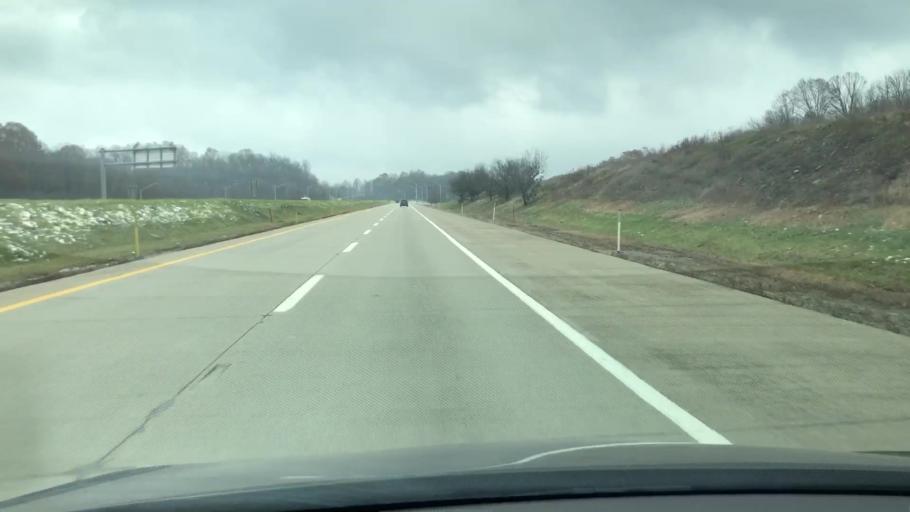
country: US
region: Pennsylvania
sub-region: Westmoreland County
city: Youngwood
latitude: 40.2758
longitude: -79.6132
